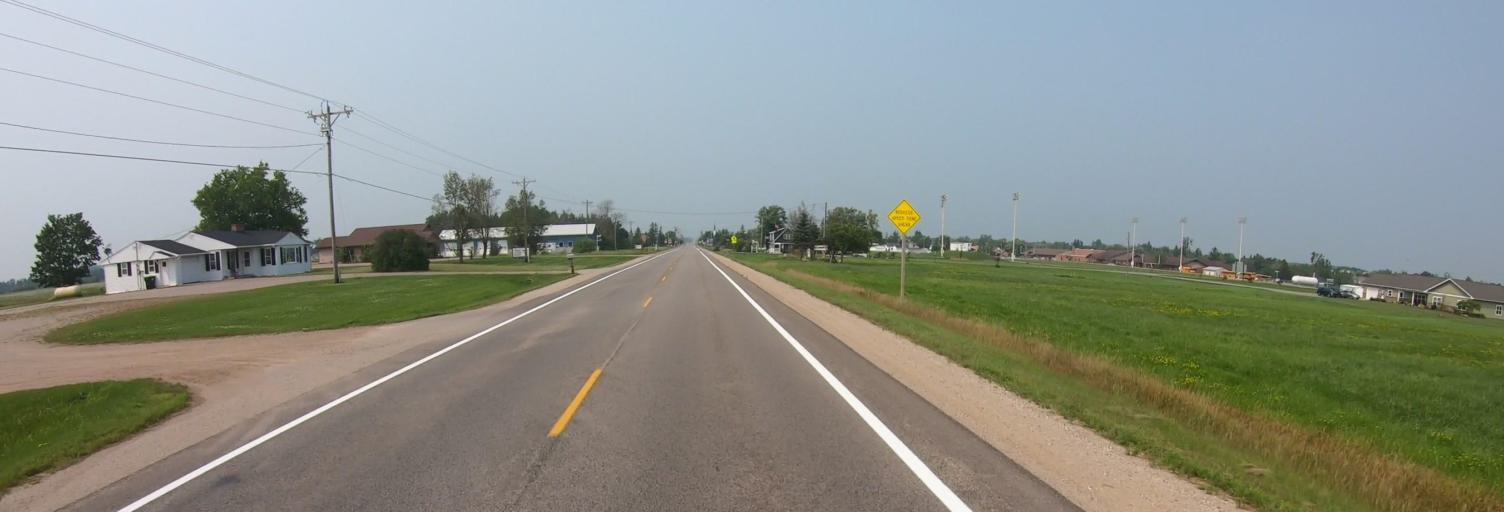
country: US
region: Michigan
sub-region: Chippewa County
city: Sault Ste. Marie
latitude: 46.1512
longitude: -84.3634
